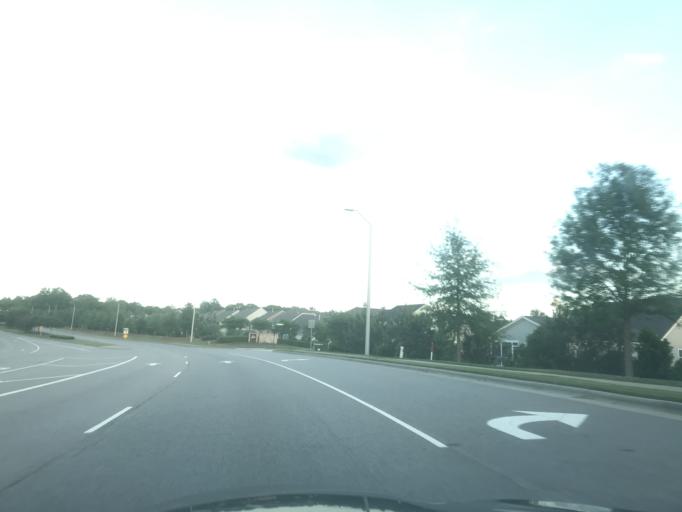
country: US
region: North Carolina
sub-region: Wake County
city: Wendell
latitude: 35.7696
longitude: -78.4232
